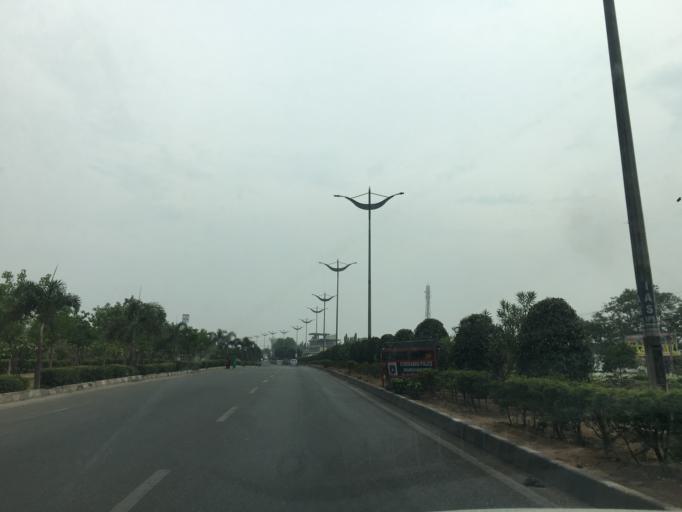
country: IN
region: Telangana
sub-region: Rangareddi
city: Balapur
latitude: 17.2962
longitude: 78.4182
